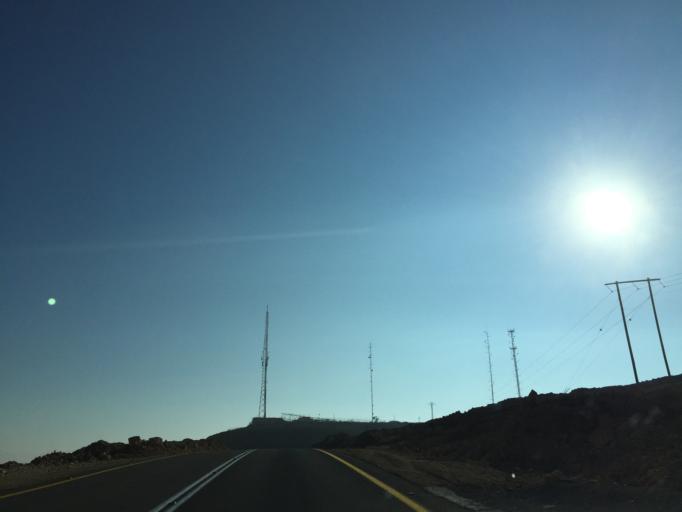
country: JO
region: Ma'an
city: Al Quwayrah
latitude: 30.0215
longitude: 35.0558
